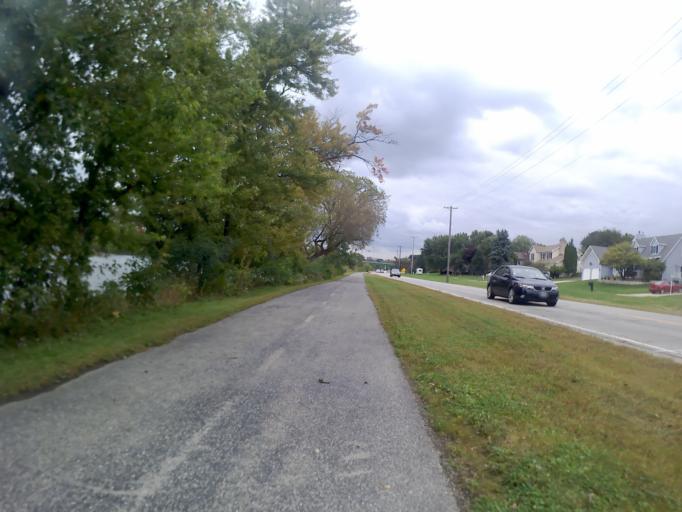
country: US
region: Illinois
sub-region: Kendall County
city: Boulder Hill
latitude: 41.7177
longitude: -88.3462
